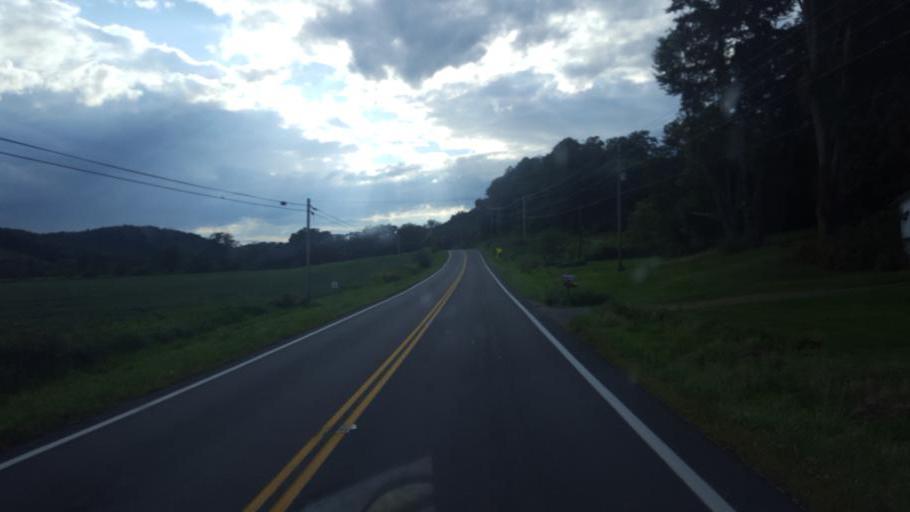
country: US
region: Ohio
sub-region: Holmes County
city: Millersburg
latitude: 40.4820
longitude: -82.0379
